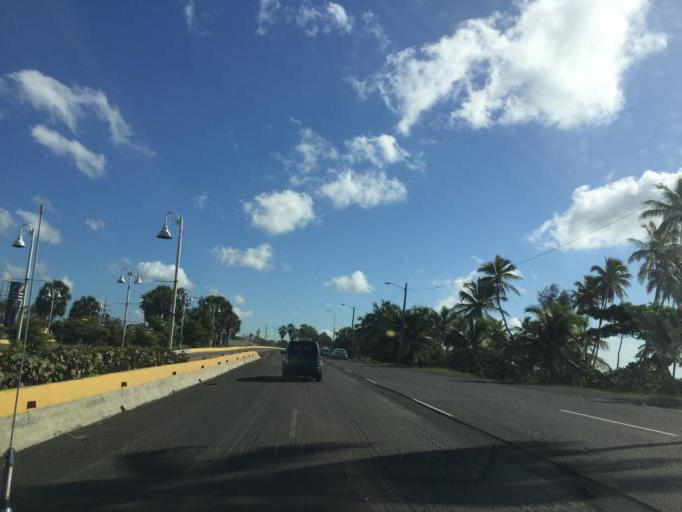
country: DO
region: Santo Domingo
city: Guerra
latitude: 18.4555
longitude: -69.7077
